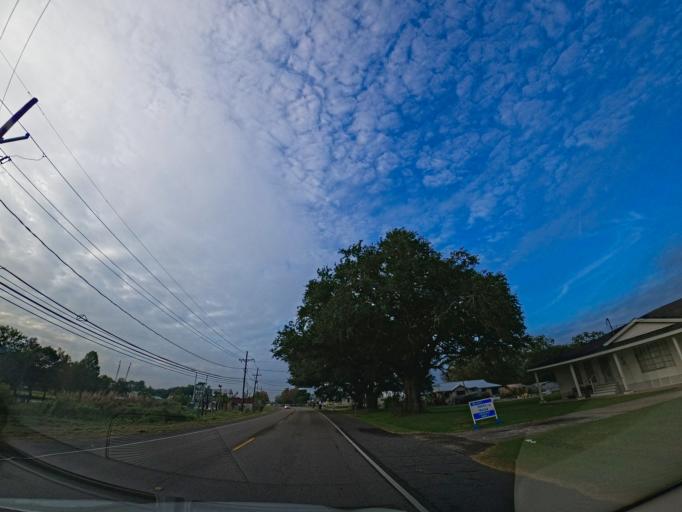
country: US
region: Louisiana
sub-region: Terrebonne Parish
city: Chauvin
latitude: 29.4479
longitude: -90.5938
